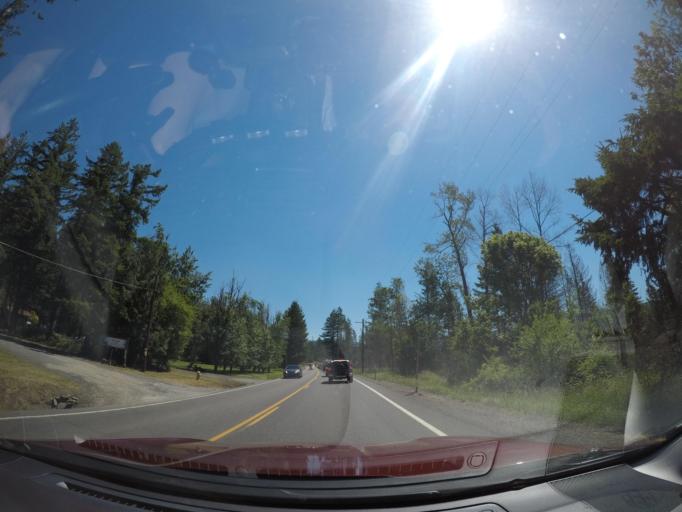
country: US
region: Oregon
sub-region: Linn County
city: Mill City
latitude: 44.7556
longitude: -122.4120
